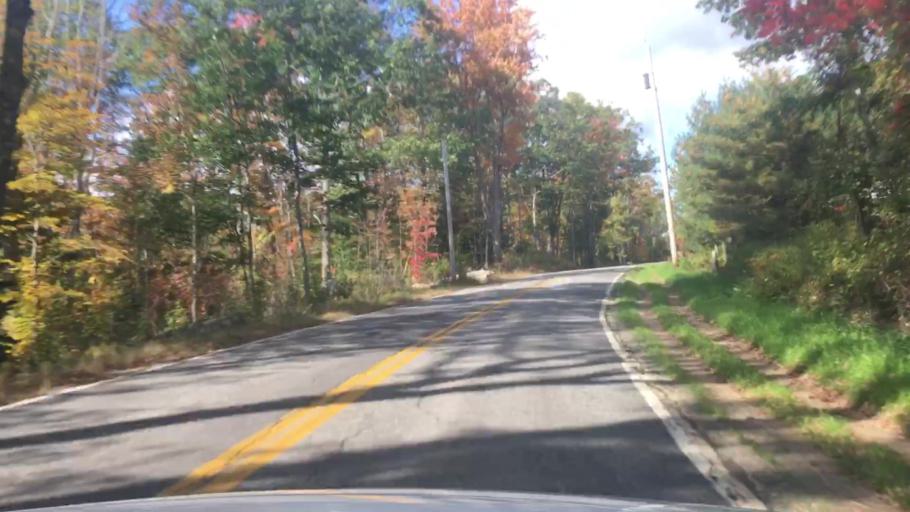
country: US
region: Maine
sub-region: Knox County
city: Appleton
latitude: 44.2700
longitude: -69.2826
